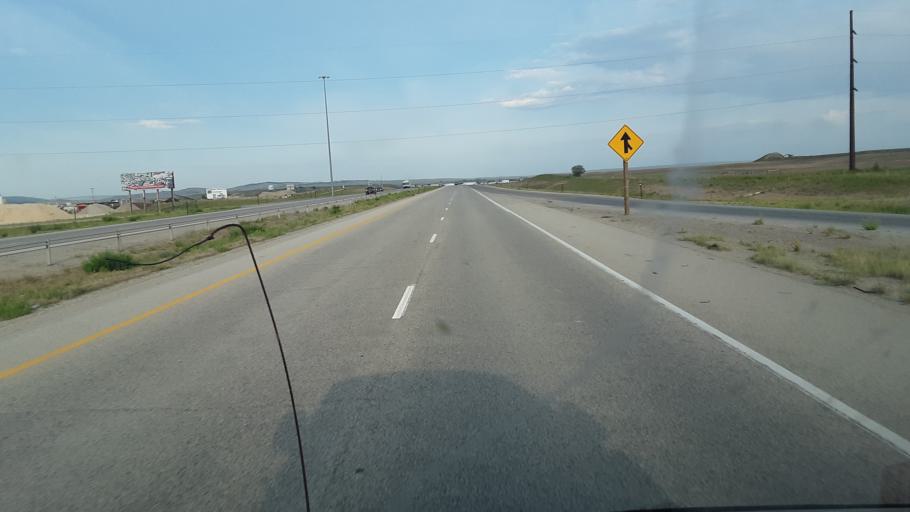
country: US
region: Wyoming
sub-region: Natrona County
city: Mills
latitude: 42.8644
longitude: -106.3642
